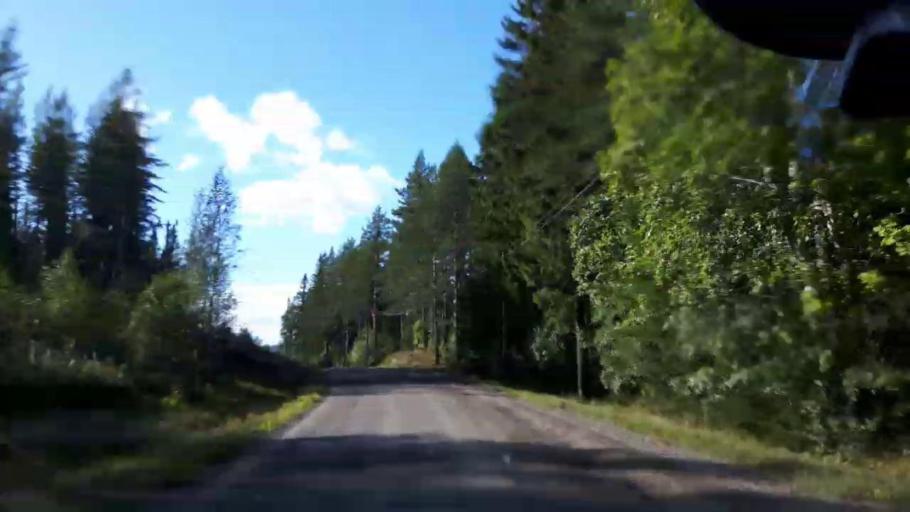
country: SE
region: Vaesternorrland
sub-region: Solleftea Kommun
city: As
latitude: 63.4624
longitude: 16.2519
